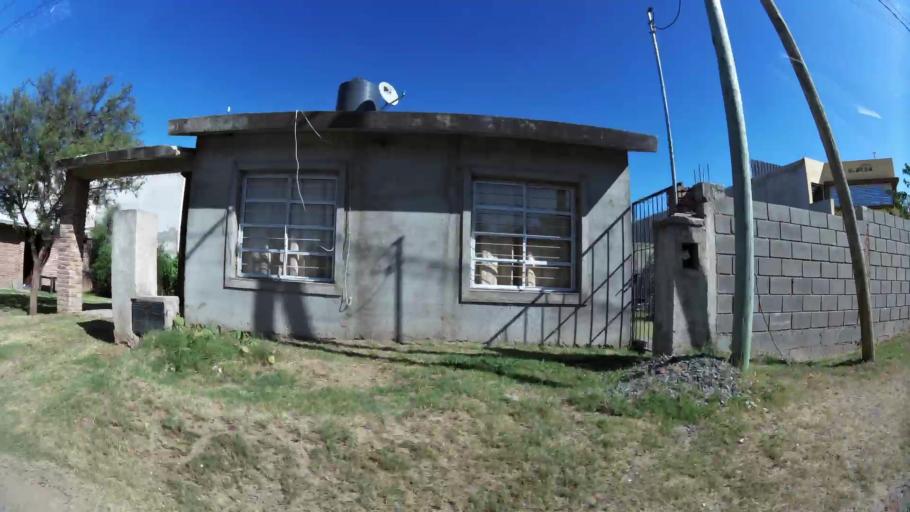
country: AR
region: Cordoba
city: La Calera
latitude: -31.3579
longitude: -64.3105
